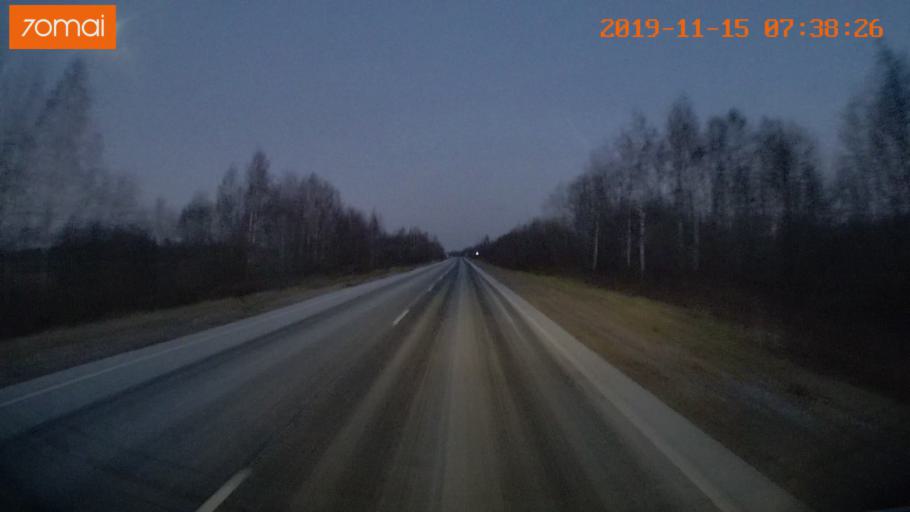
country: RU
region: Vologda
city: Sheksna
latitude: 58.7572
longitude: 38.4014
